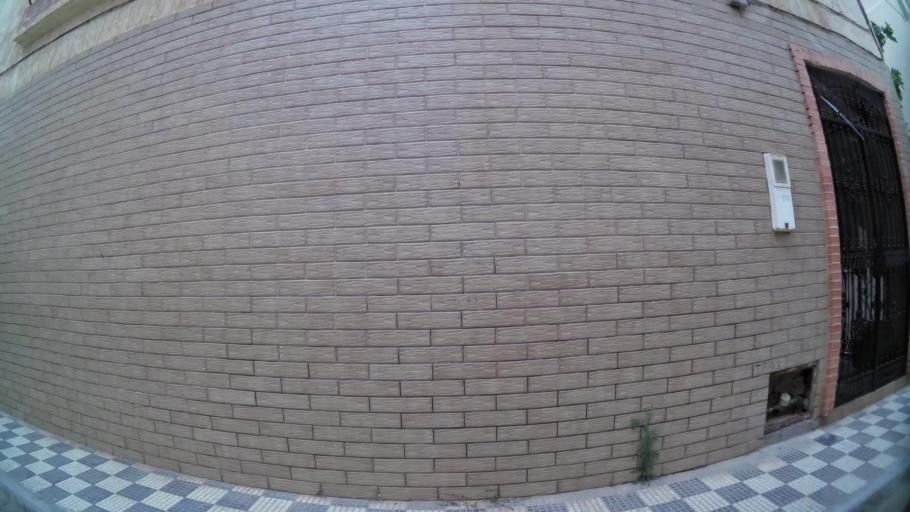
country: MA
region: Oriental
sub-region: Nador
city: Nador
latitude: 35.1730
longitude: -2.9312
